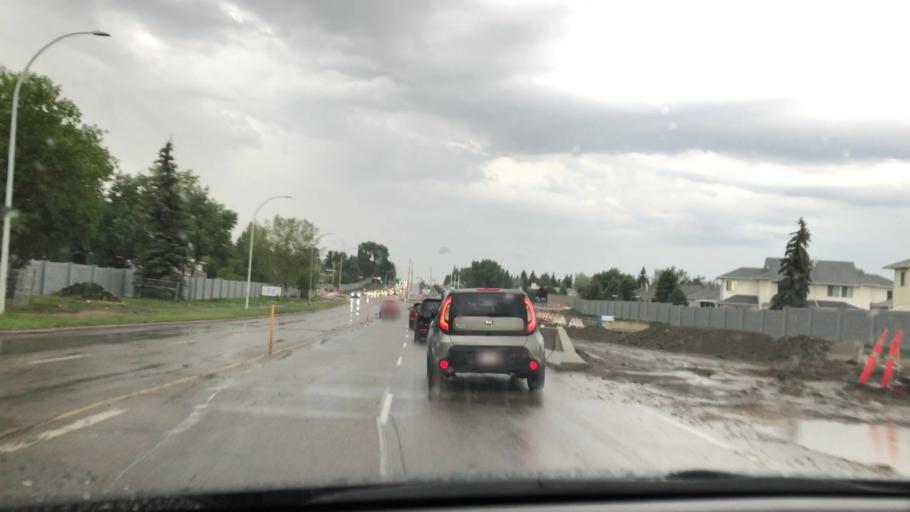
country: CA
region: Alberta
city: Edmonton
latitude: 53.4631
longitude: -113.4350
